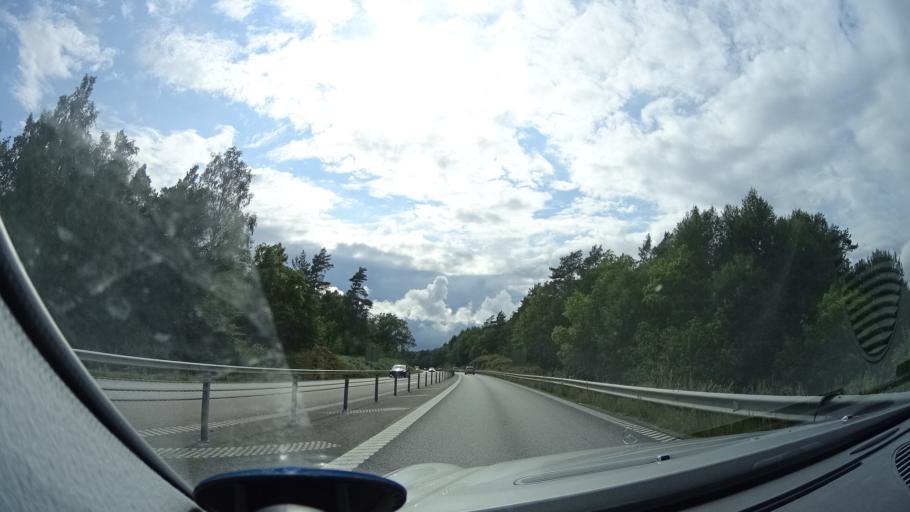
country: SE
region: Blekinge
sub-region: Karlshamns Kommun
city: Morrum
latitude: 56.1902
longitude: 14.7964
